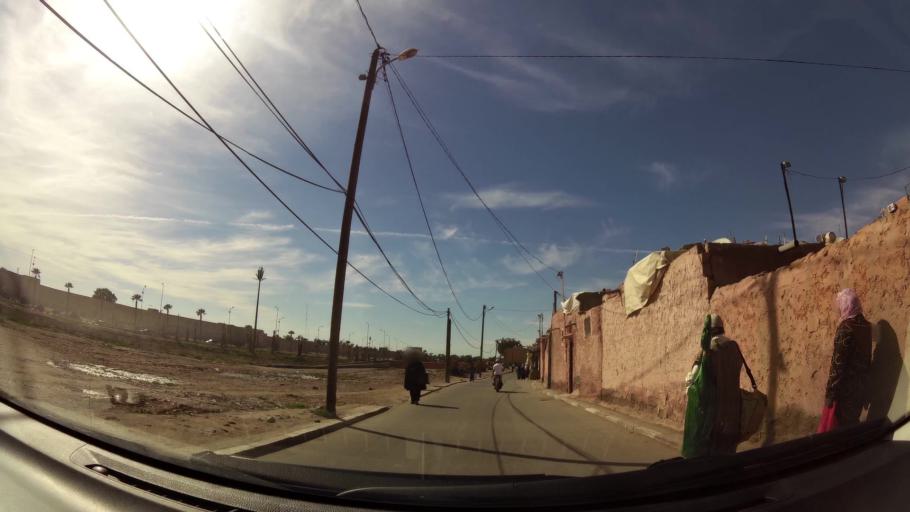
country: MA
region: Marrakech-Tensift-Al Haouz
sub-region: Marrakech
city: Marrakesh
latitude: 31.6381
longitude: -7.9794
